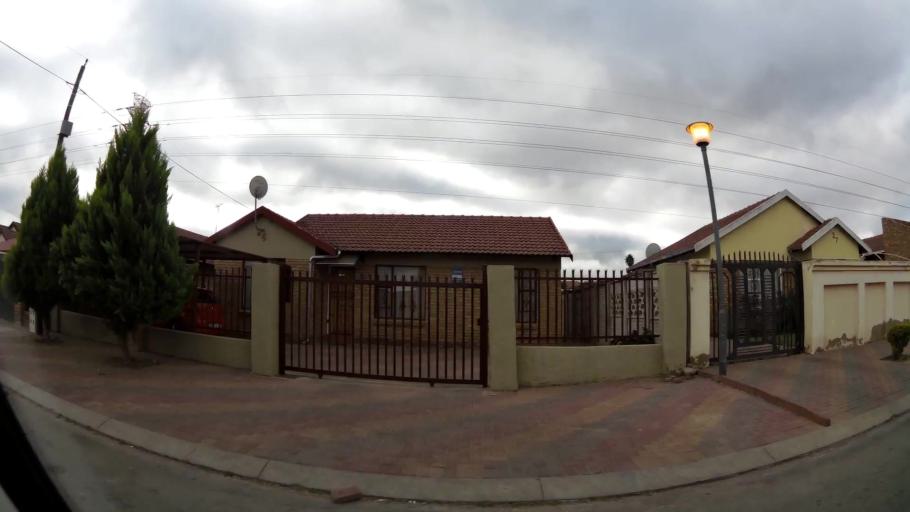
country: ZA
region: Limpopo
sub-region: Capricorn District Municipality
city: Polokwane
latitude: -23.9197
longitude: 29.4498
